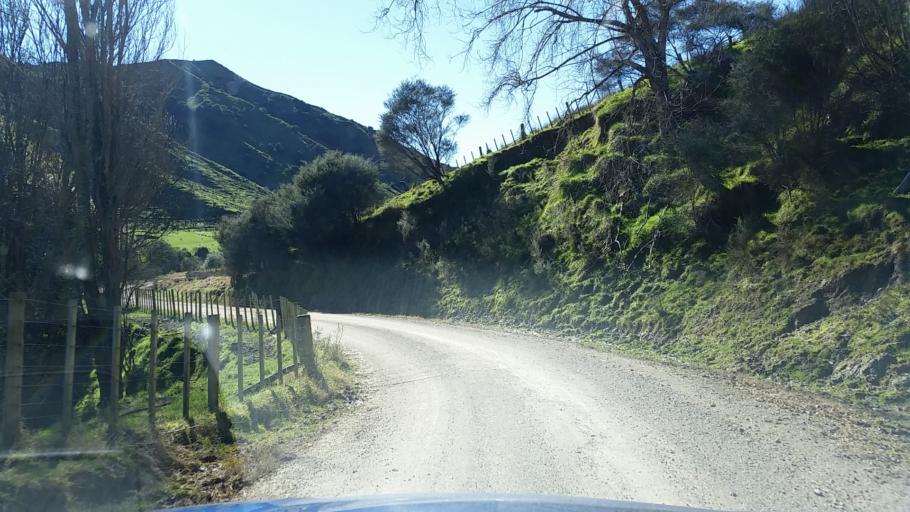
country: NZ
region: Manawatu-Wanganui
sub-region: Wanganui District
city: Wanganui
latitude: -39.5430
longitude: 174.9070
